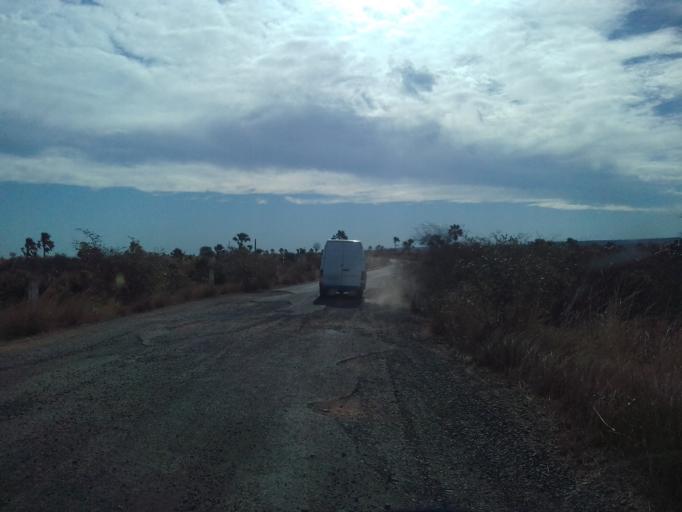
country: MG
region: Sofia
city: Antsohihy
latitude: -15.3579
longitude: 47.7632
